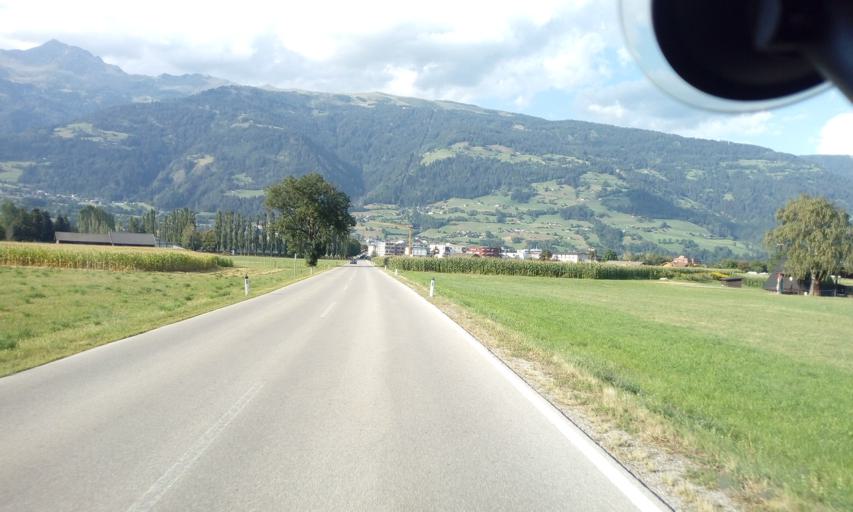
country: AT
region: Tyrol
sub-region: Politischer Bezirk Lienz
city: Amlach
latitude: 46.8188
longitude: 12.7665
